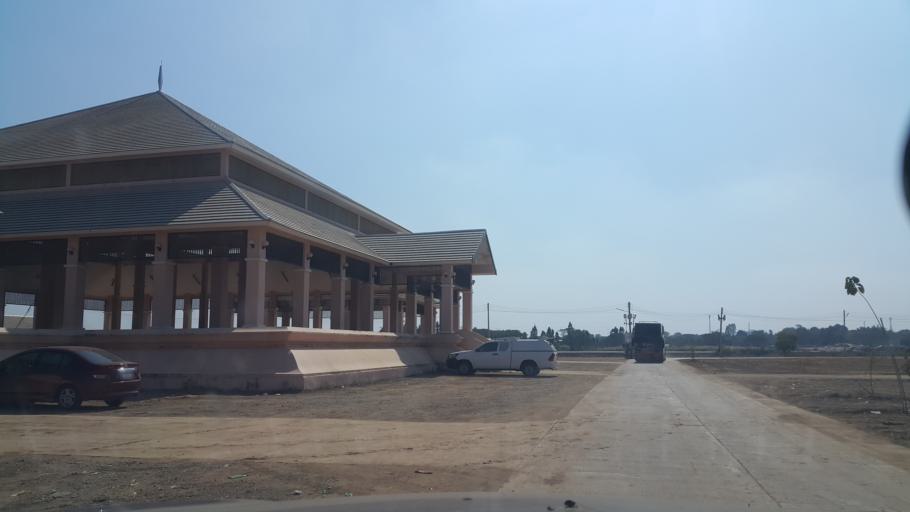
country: TH
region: Khon Kaen
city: Khon Kaen
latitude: 16.5107
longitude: 102.8714
